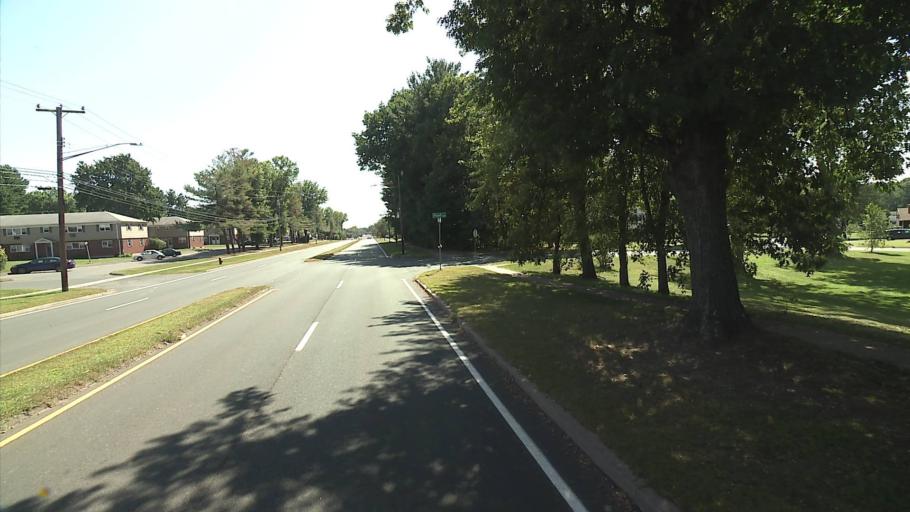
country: US
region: Connecticut
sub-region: Hartford County
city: Windsor
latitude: 41.8256
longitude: -72.6563
